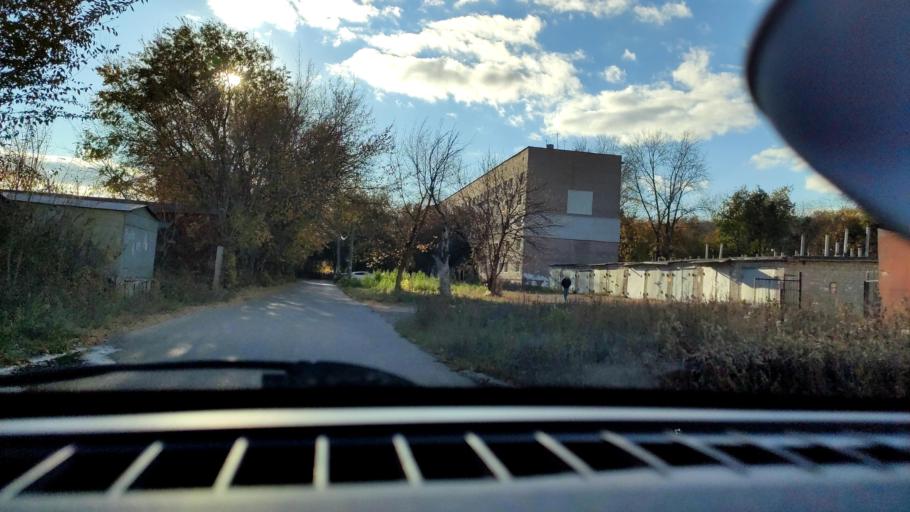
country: RU
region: Samara
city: Smyshlyayevka
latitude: 53.2165
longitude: 50.2754
